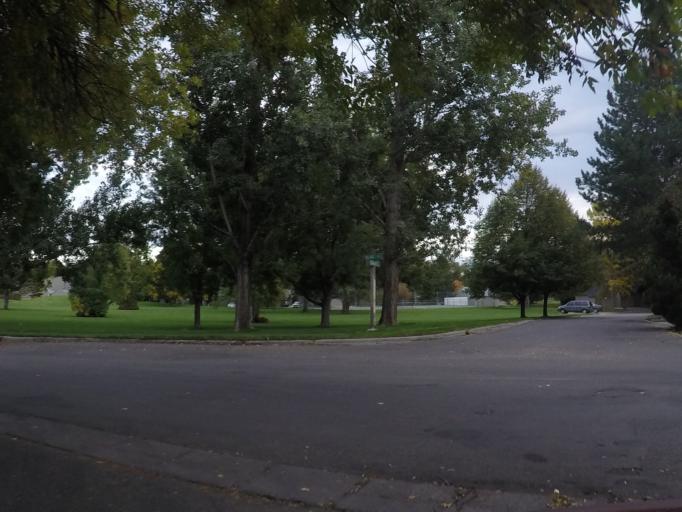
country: US
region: Montana
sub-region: Yellowstone County
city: Billings
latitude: 45.7934
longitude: -108.5558
